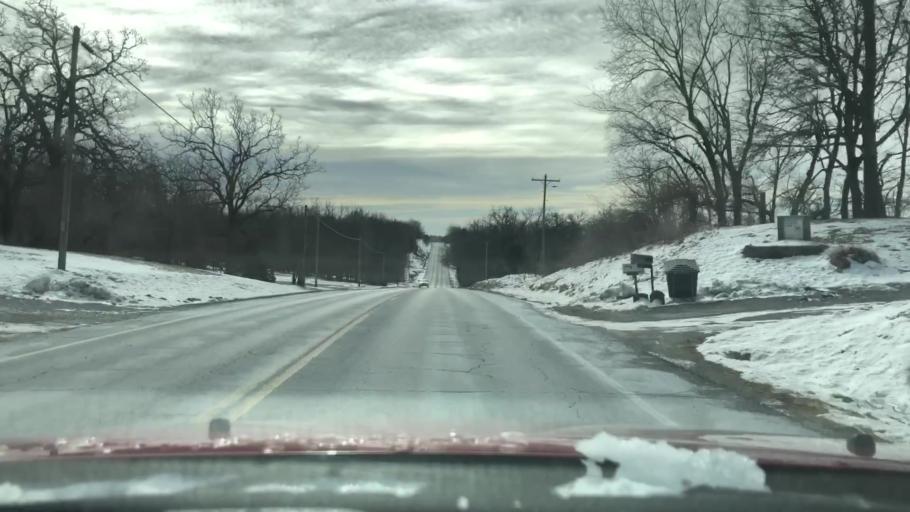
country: US
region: Missouri
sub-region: Jackson County
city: Oak Grove
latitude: 38.9739
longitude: -94.1306
